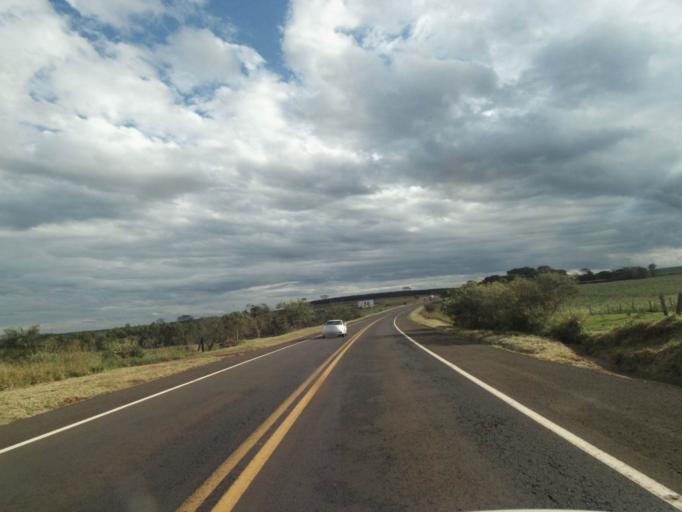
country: PY
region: Canindeyu
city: Salto del Guaira
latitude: -24.0825
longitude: -54.0678
